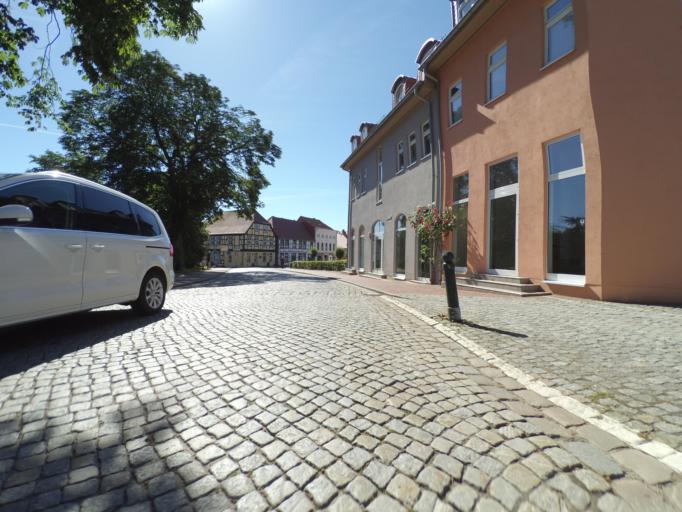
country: DE
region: Mecklenburg-Vorpommern
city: Plau am See
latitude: 53.4588
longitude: 12.2652
